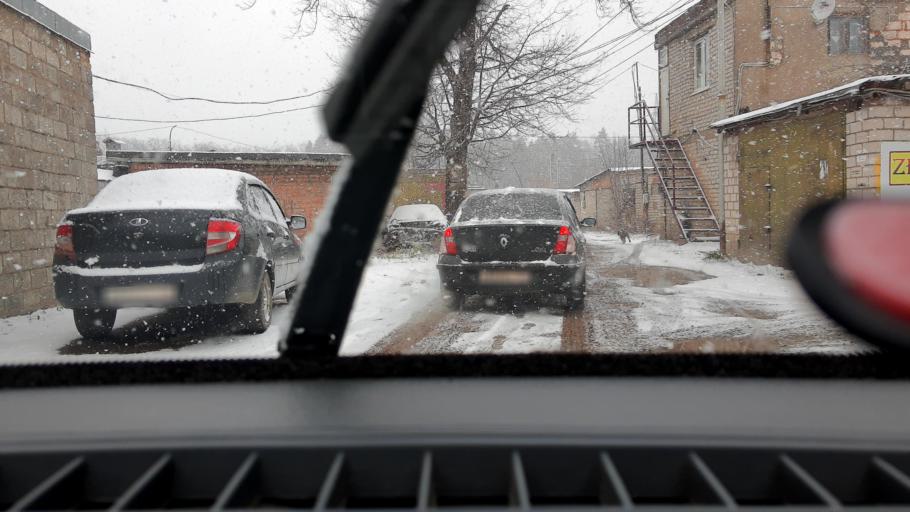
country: RU
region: Bashkortostan
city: Ufa
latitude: 54.8019
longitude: 56.0401
